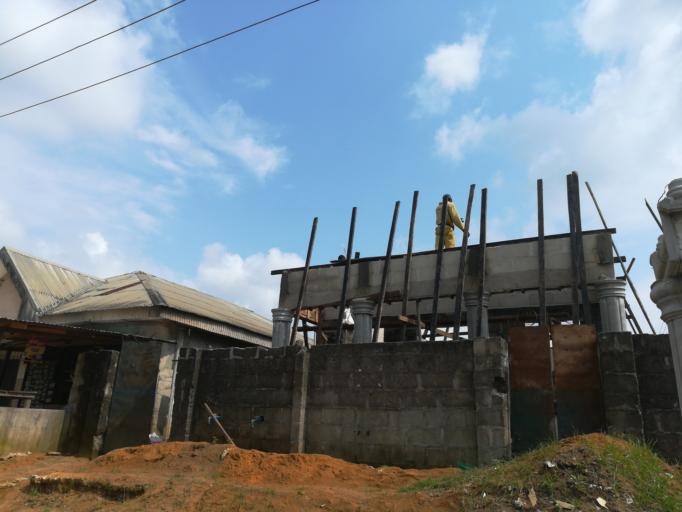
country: NG
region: Rivers
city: Okrika
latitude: 4.7437
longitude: 7.1143
